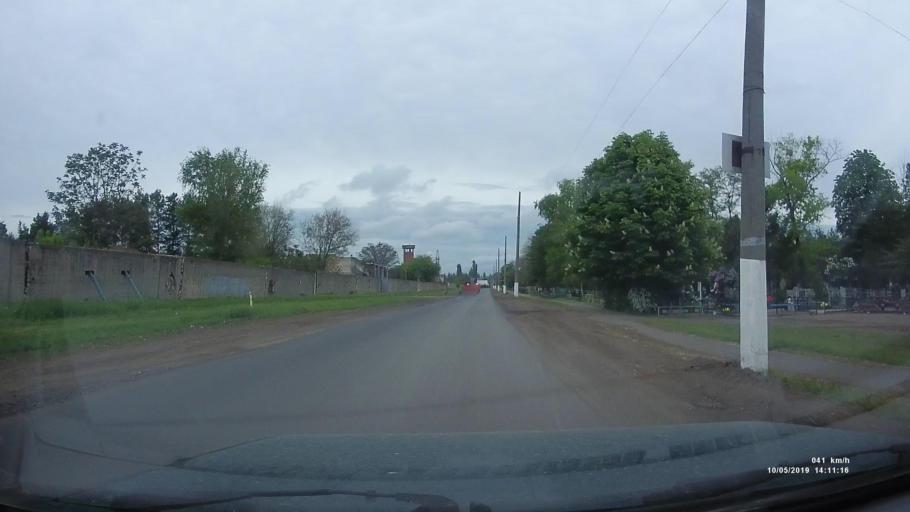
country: RU
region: Rostov
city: Azov
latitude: 47.0925
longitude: 39.4164
